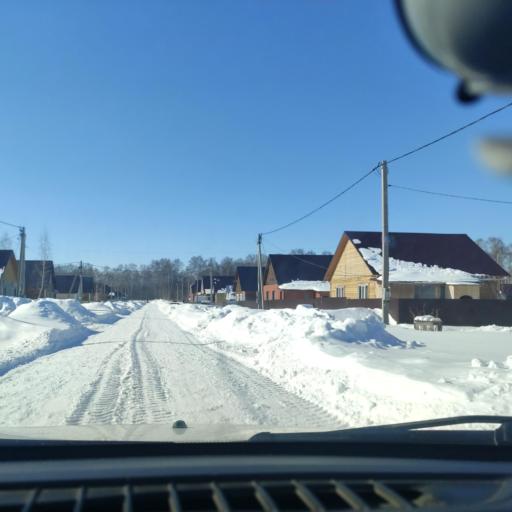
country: RU
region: Bashkortostan
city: Iglino
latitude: 54.8111
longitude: 56.3763
